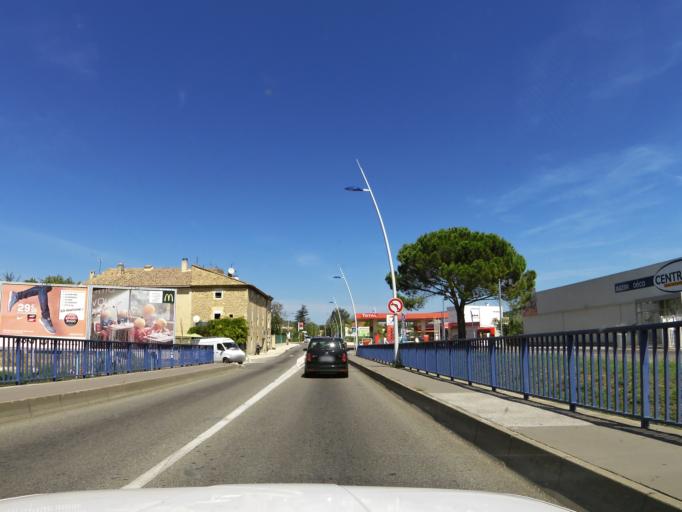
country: FR
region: Languedoc-Roussillon
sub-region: Departement du Gard
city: Bagnols-sur-Ceze
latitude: 44.1710
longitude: 4.6201
